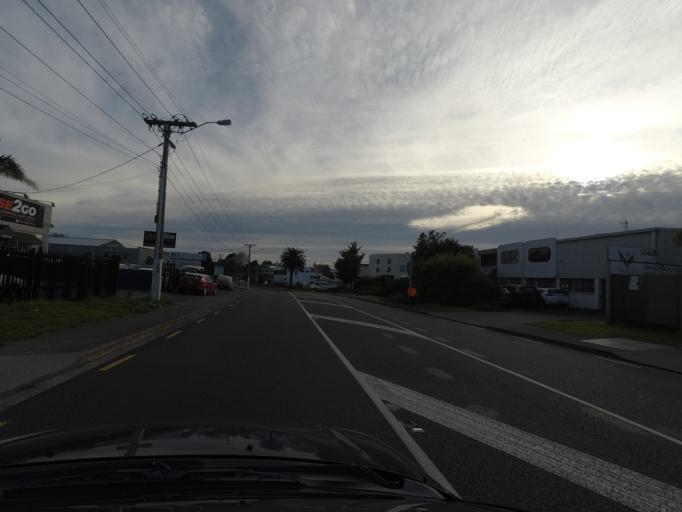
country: NZ
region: Auckland
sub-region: Auckland
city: Tamaki
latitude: -36.8921
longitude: 174.8311
